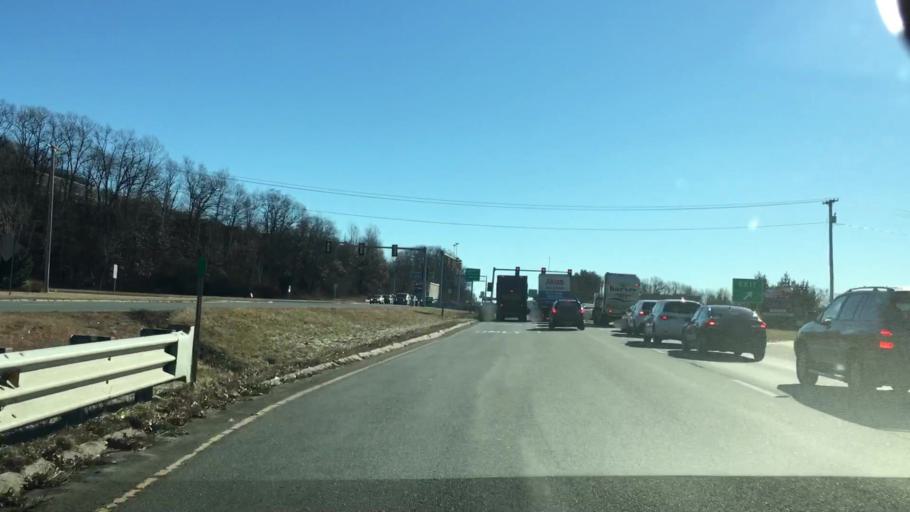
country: US
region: Massachusetts
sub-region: Essex County
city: Haverhill
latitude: 42.7571
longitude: -71.1156
